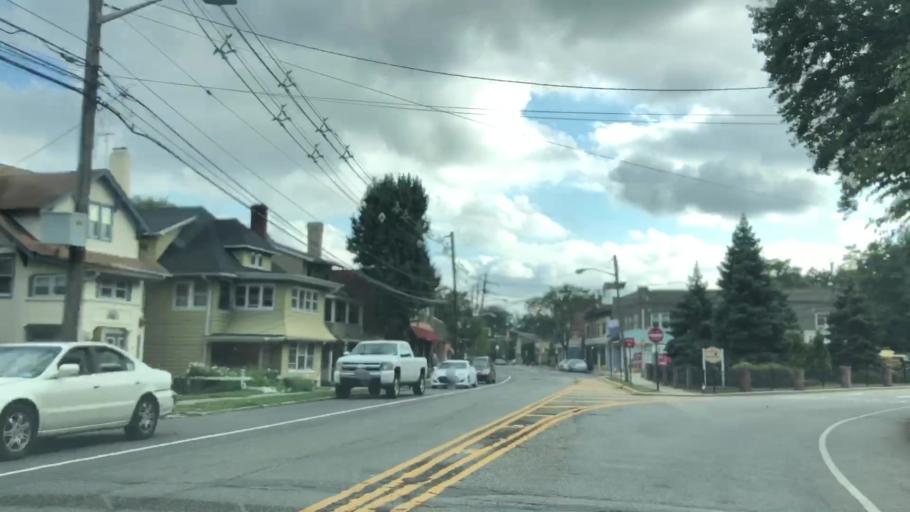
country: US
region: New Jersey
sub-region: Essex County
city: Glen Ridge
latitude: 40.7987
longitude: -74.2190
